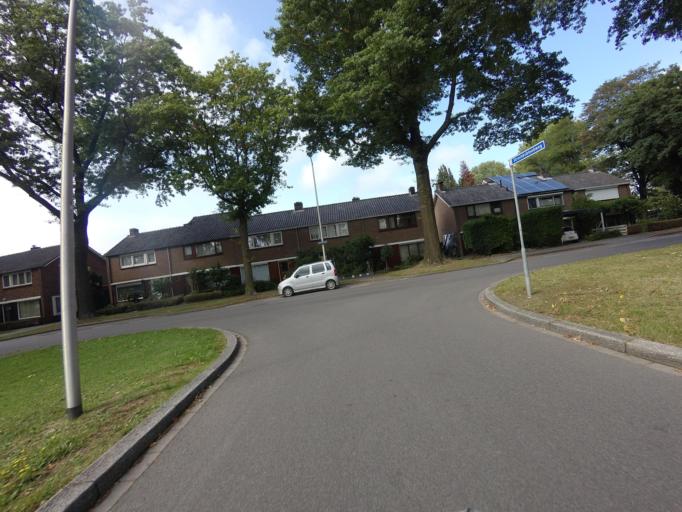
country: NL
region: Overijssel
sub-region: Gemeente Enschede
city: Enschede
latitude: 52.2377
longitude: 6.8960
